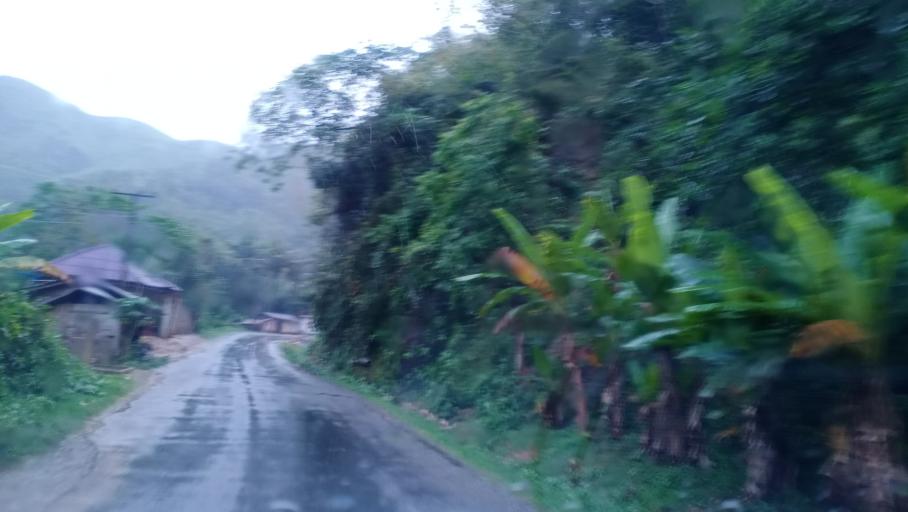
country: LA
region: Phongsali
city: Khoa
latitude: 21.0595
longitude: 102.4643
